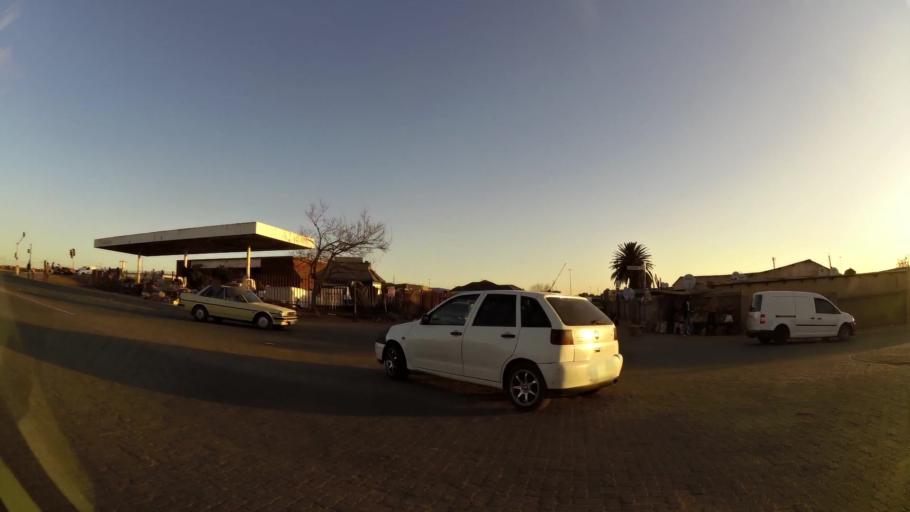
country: ZA
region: Gauteng
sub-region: Ekurhuleni Metropolitan Municipality
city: Tembisa
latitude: -26.0006
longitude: 28.2224
